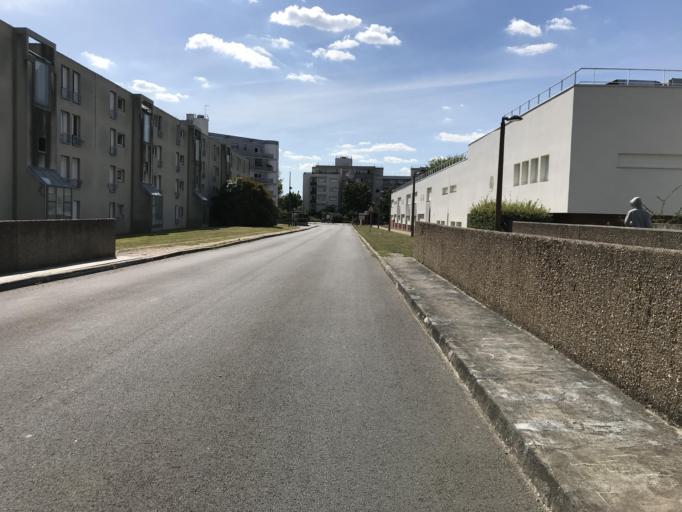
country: FR
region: Ile-de-France
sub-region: Departement de l'Essonne
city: Ris-Orangis
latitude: 48.6381
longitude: 2.4221
